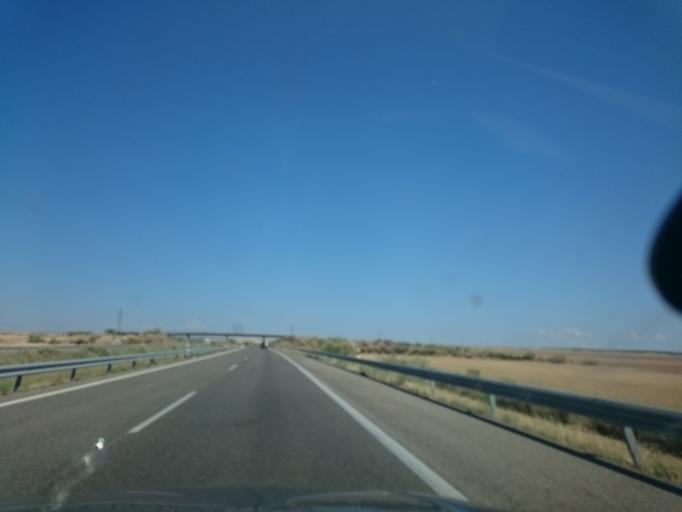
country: ES
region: Aragon
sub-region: Provincia de Zaragoza
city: Mequinensa / Mequinenza
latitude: 41.4716
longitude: 0.2172
